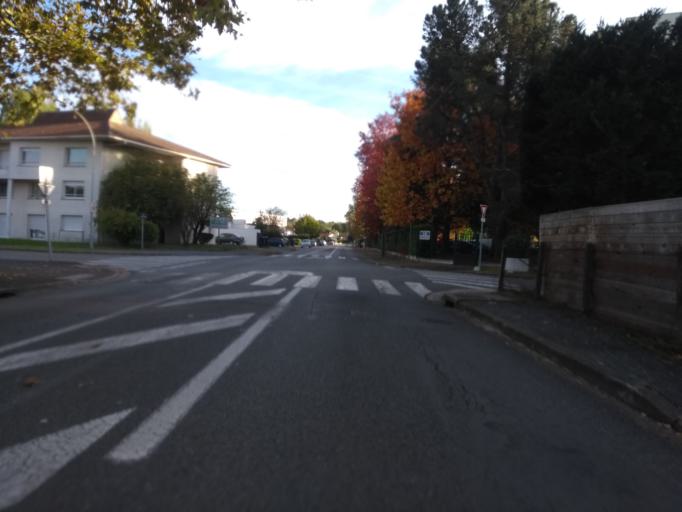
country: FR
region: Aquitaine
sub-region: Departement de la Gironde
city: Pessac
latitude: 44.7913
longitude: -0.6406
